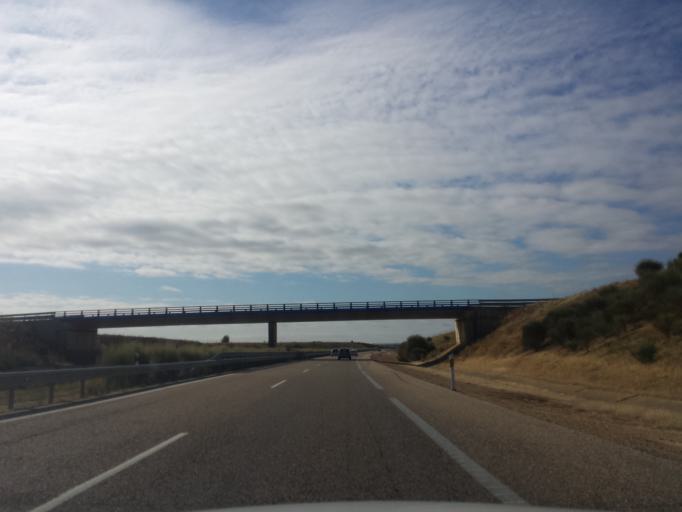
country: ES
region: Castille and Leon
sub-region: Provincia de Leon
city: Villamanan
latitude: 42.3048
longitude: -5.5933
